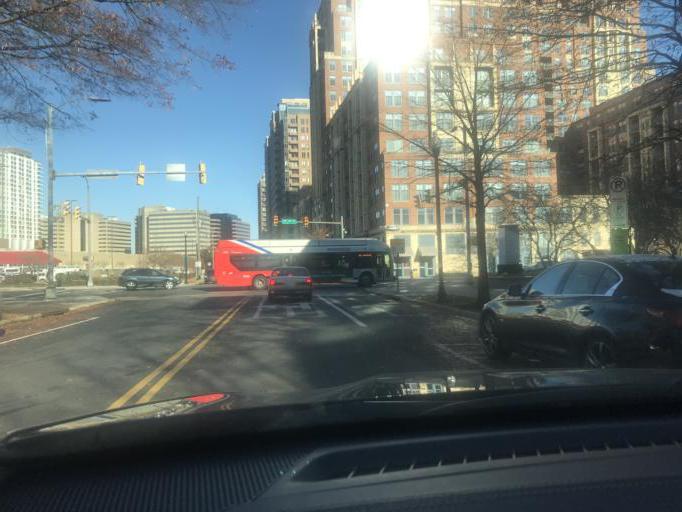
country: US
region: Washington, D.C.
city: Washington, D.C.
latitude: 38.8593
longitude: -77.0560
